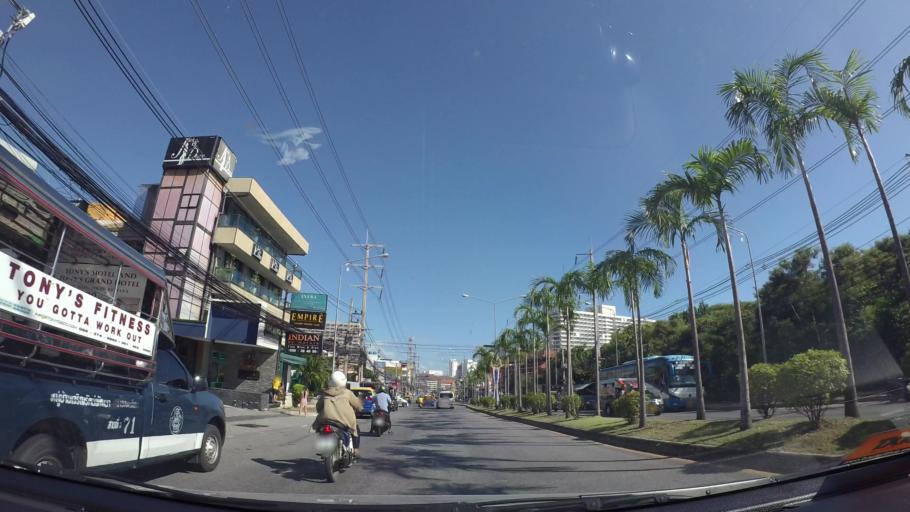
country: TH
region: Chon Buri
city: Phatthaya
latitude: 12.9060
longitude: 100.8691
